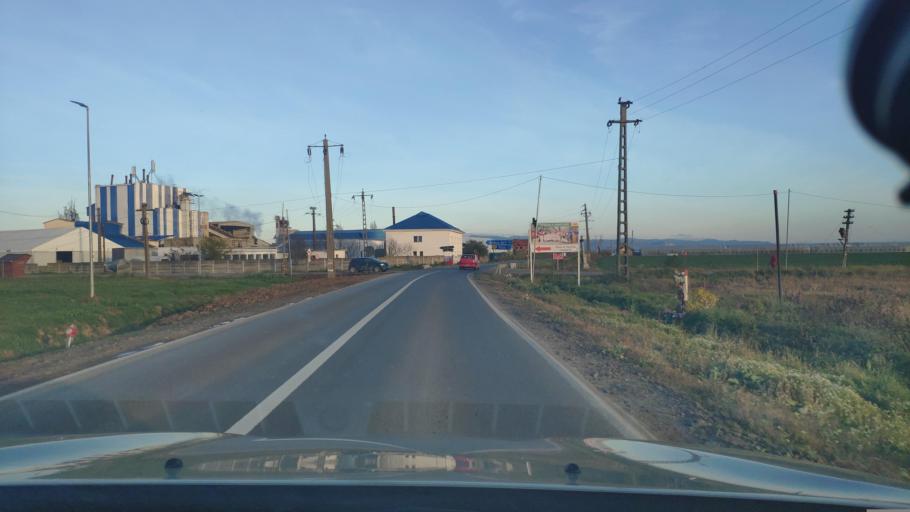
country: RO
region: Satu Mare
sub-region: Comuna Mediesu Aurit
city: Potau
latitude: 47.7730
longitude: 23.1228
